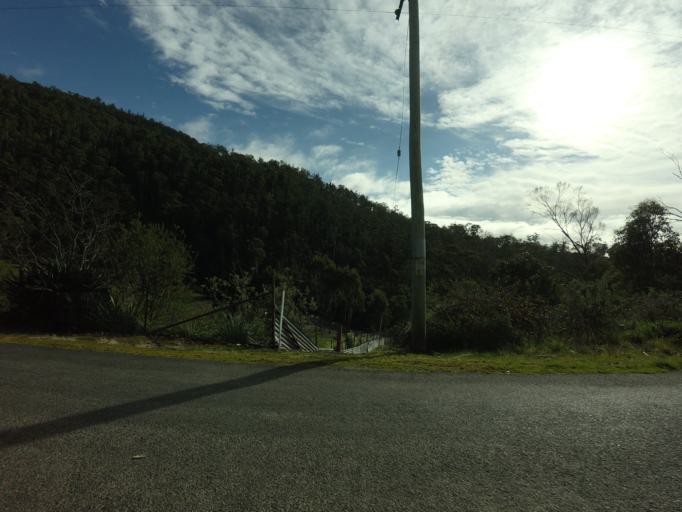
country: AU
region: Tasmania
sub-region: Derwent Valley
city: New Norfolk
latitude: -42.7810
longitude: 146.9497
